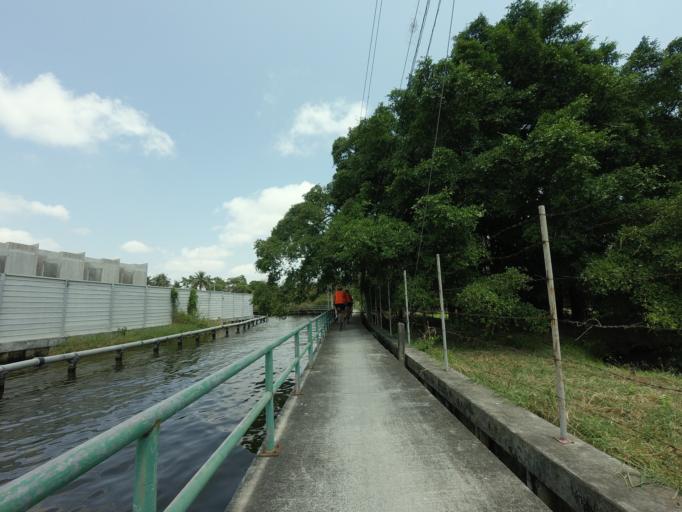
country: TH
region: Bangkok
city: Thung Khru
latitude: 13.6271
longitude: 100.4740
